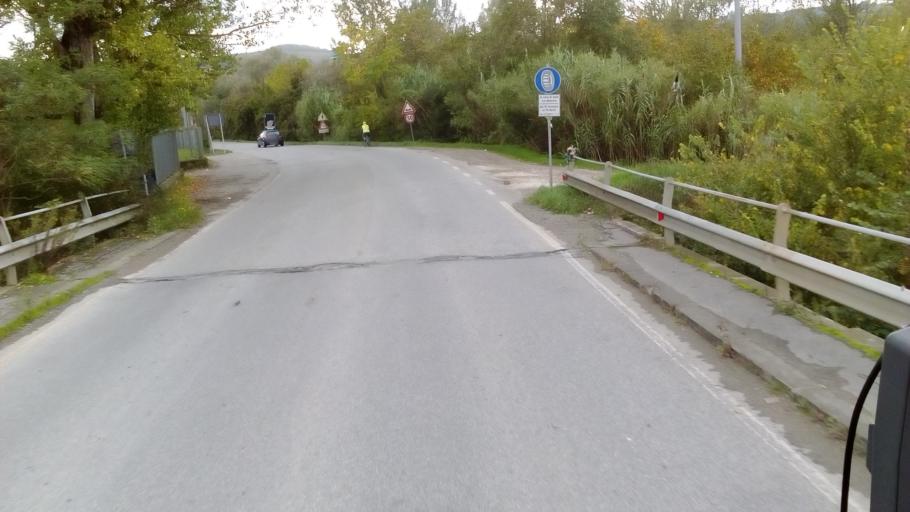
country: IT
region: Tuscany
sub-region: Province of Florence
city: Ginestra Fiorentina
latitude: 43.7070
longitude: 11.0706
